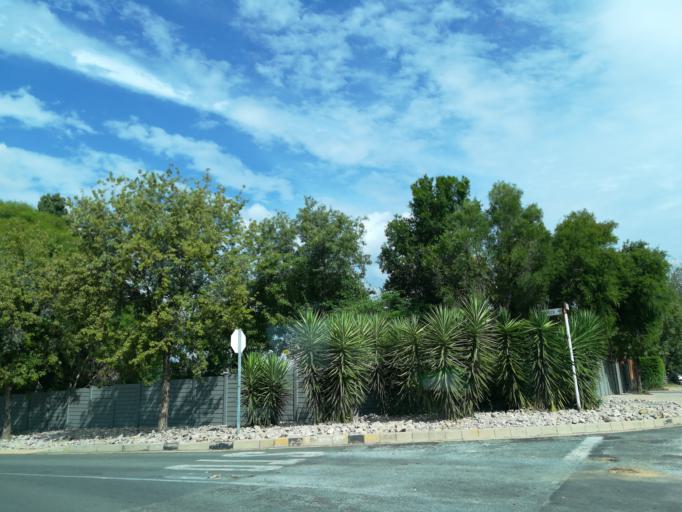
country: ZA
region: Gauteng
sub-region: City of Johannesburg Metropolitan Municipality
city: Diepsloot
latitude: -26.0548
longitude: 27.9756
